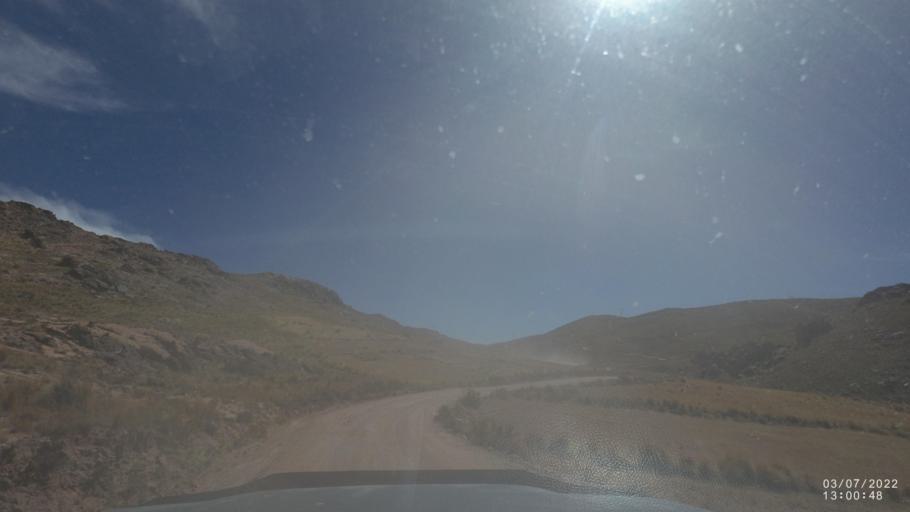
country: BO
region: Cochabamba
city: Colchani
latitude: -17.7124
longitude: -66.6897
